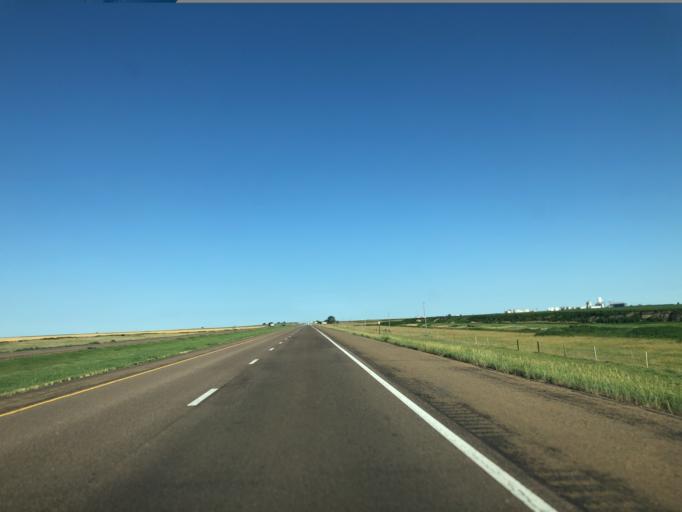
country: US
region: Kansas
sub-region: Logan County
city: Oakley
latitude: 39.1122
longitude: -100.7083
